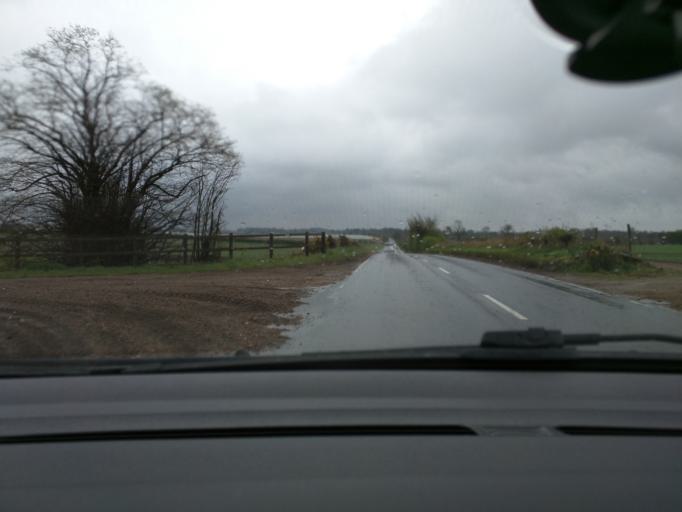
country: GB
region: England
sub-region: Suffolk
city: Saxmundham
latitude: 52.1799
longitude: 1.5189
